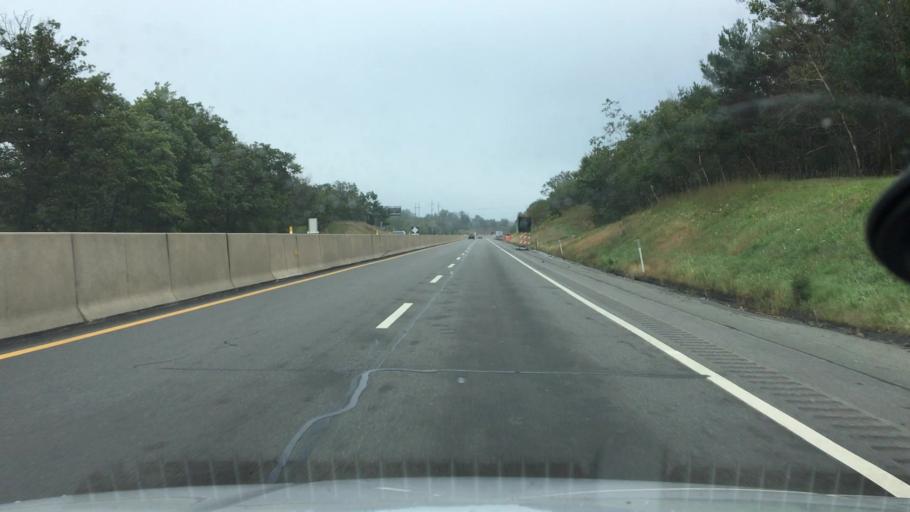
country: US
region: Pennsylvania
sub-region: Luzerne County
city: Hudson
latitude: 41.2219
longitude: -75.7985
